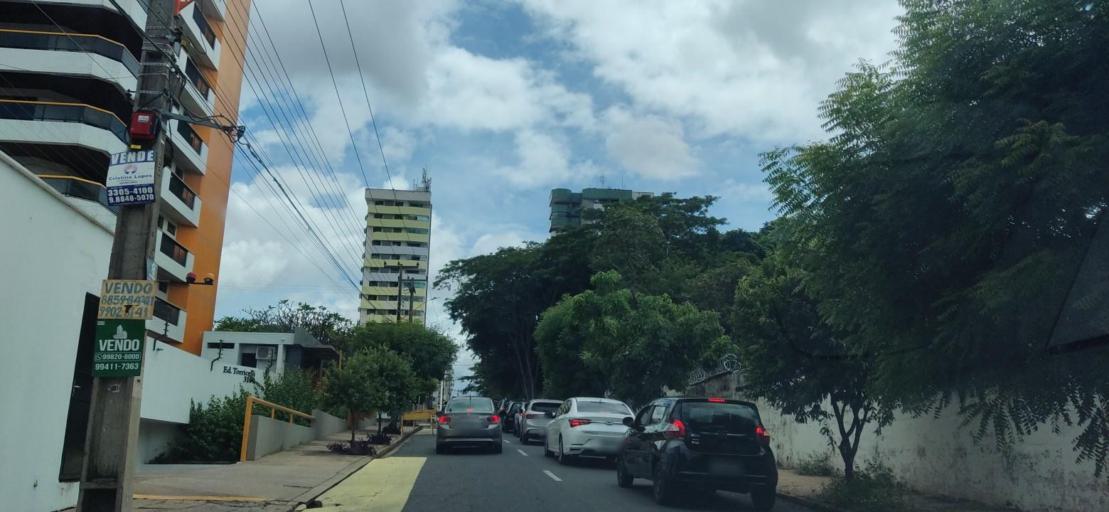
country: BR
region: Piaui
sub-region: Teresina
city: Teresina
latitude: -5.0847
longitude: -42.7970
